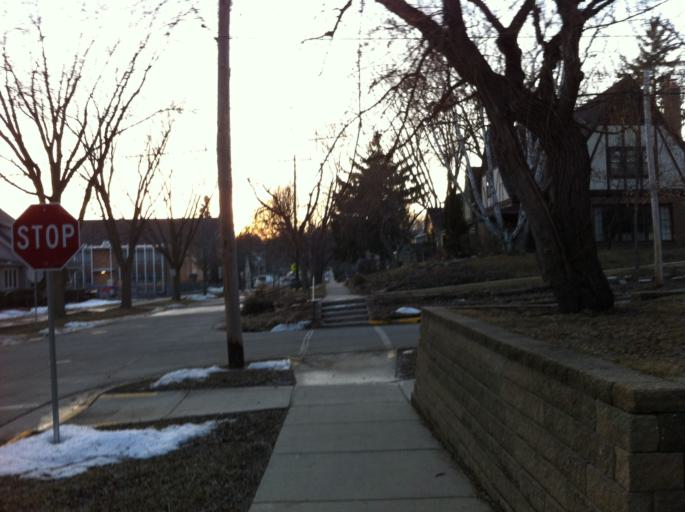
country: US
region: Wisconsin
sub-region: Dane County
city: Madison
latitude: 43.0671
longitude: -89.4210
